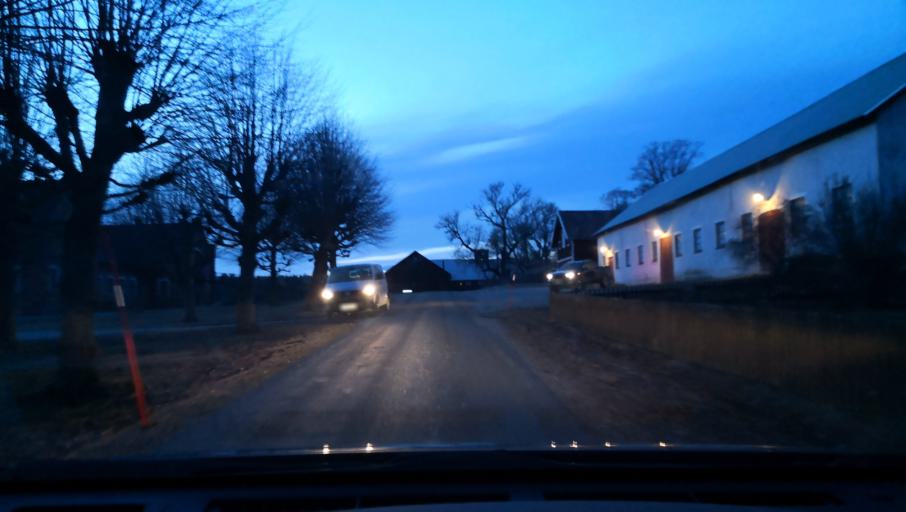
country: SE
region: Uppsala
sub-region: Enkopings Kommun
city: Dalby
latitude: 59.5746
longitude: 17.3776
